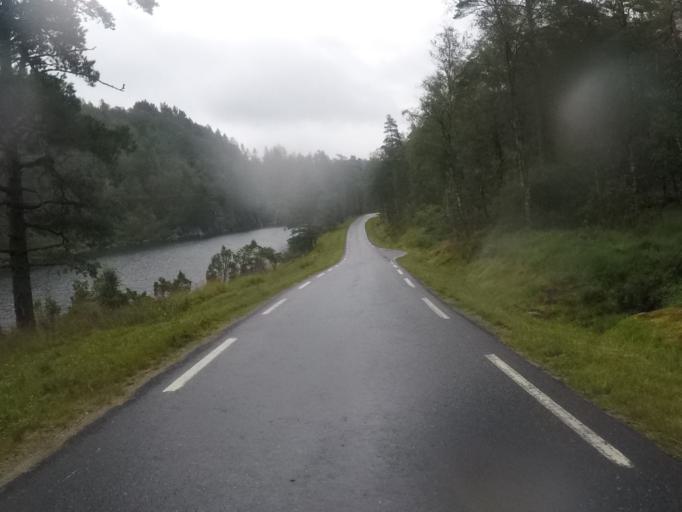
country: NO
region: Vest-Agder
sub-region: Lyngdal
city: Lyngdal
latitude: 58.2488
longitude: 7.0787
